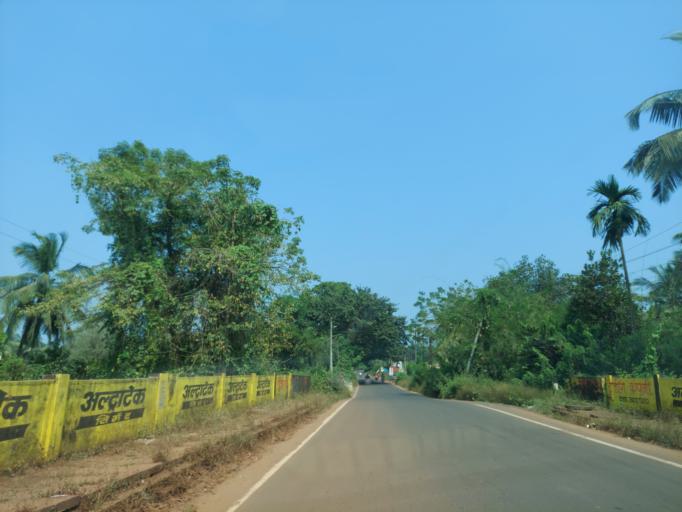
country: IN
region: Maharashtra
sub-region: Sindhudurg
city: Kudal
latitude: 15.9932
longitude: 73.6844
